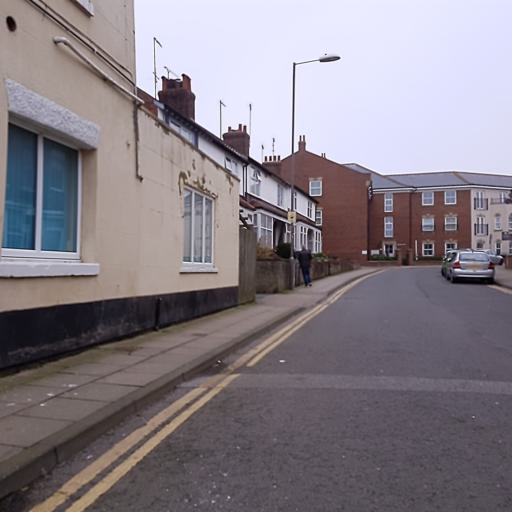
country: GB
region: England
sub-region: North Yorkshire
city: Filey
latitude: 54.2099
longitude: -0.2868
